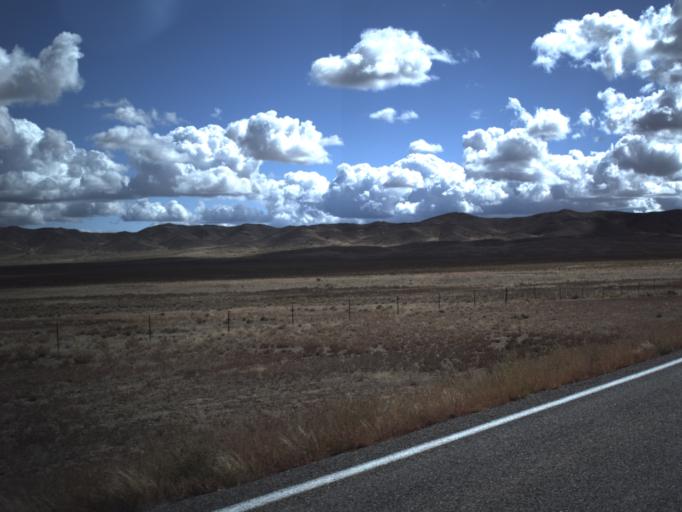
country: US
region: Utah
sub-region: Beaver County
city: Milford
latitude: 38.6655
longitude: -113.8807
